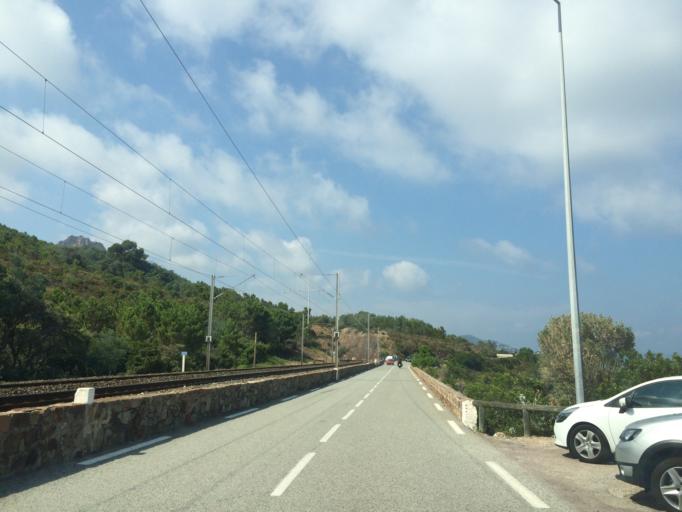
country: FR
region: Provence-Alpes-Cote d'Azur
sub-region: Departement des Alpes-Maritimes
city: Theoule-sur-Mer
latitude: 43.4526
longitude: 6.9198
